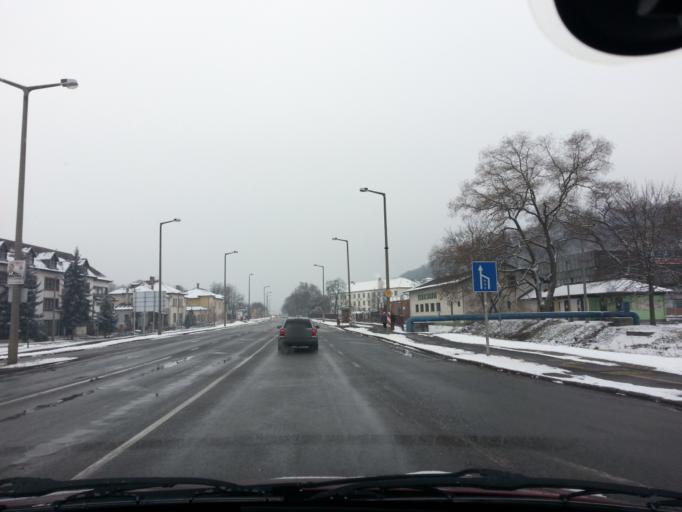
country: HU
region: Nograd
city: Salgotarjan
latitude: 48.1034
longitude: 19.8031
